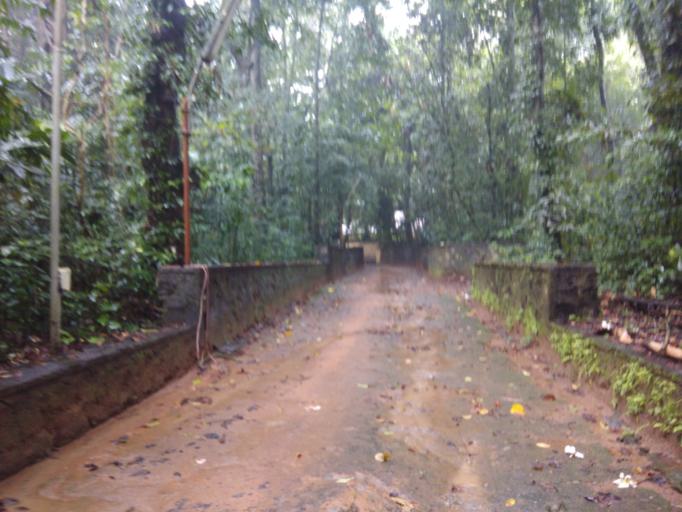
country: IN
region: Kerala
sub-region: Ernakulam
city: Perumpavur
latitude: 10.1093
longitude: 76.5002
